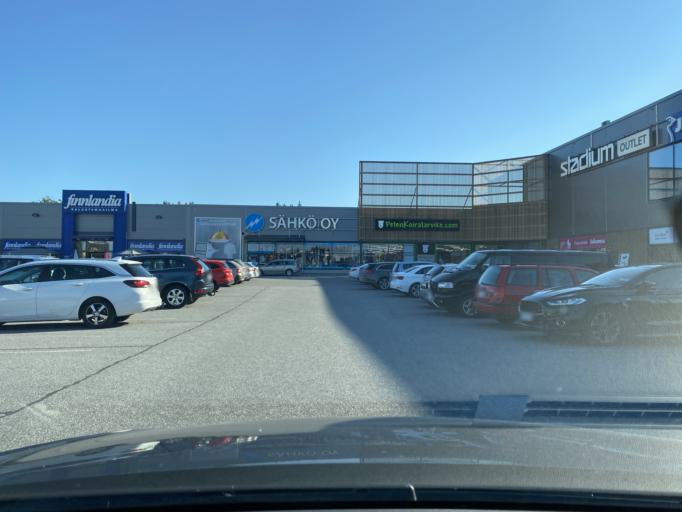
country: FI
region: Varsinais-Suomi
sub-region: Turku
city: Rusko
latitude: 60.4921
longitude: 22.2218
